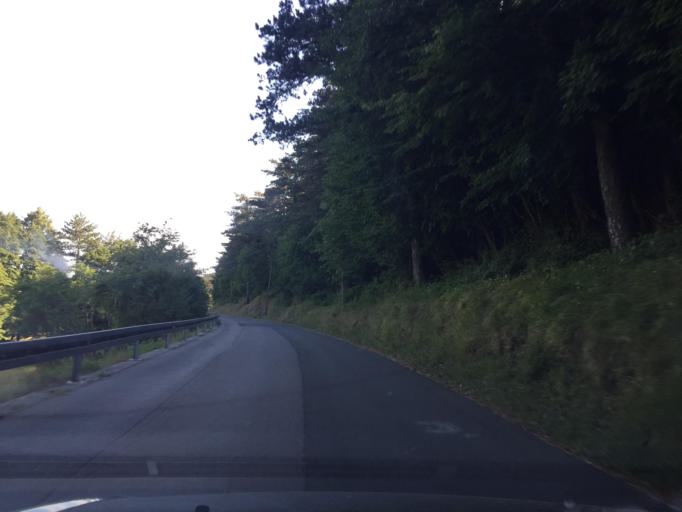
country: HR
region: Primorsko-Goranska
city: Klana
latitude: 45.4596
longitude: 14.3779
